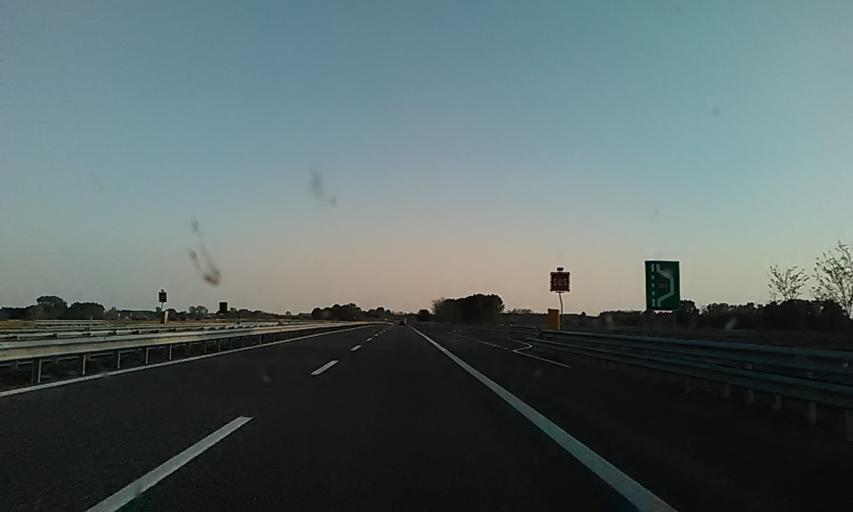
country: IT
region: Piedmont
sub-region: Provincia di Novara
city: Sillavengo
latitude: 45.5198
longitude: 8.4320
